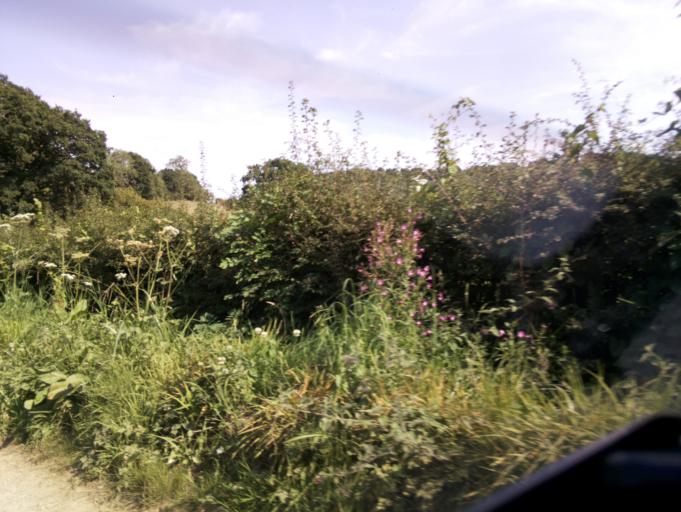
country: GB
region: England
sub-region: Gloucestershire
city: Dursley
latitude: 51.7024
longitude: -2.3168
